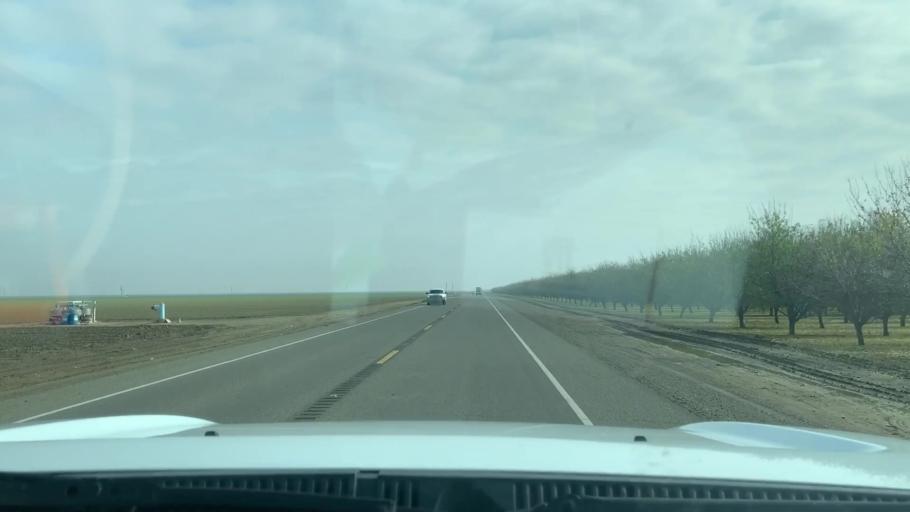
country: US
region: California
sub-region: Fresno County
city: Huron
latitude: 36.2554
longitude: -120.0400
